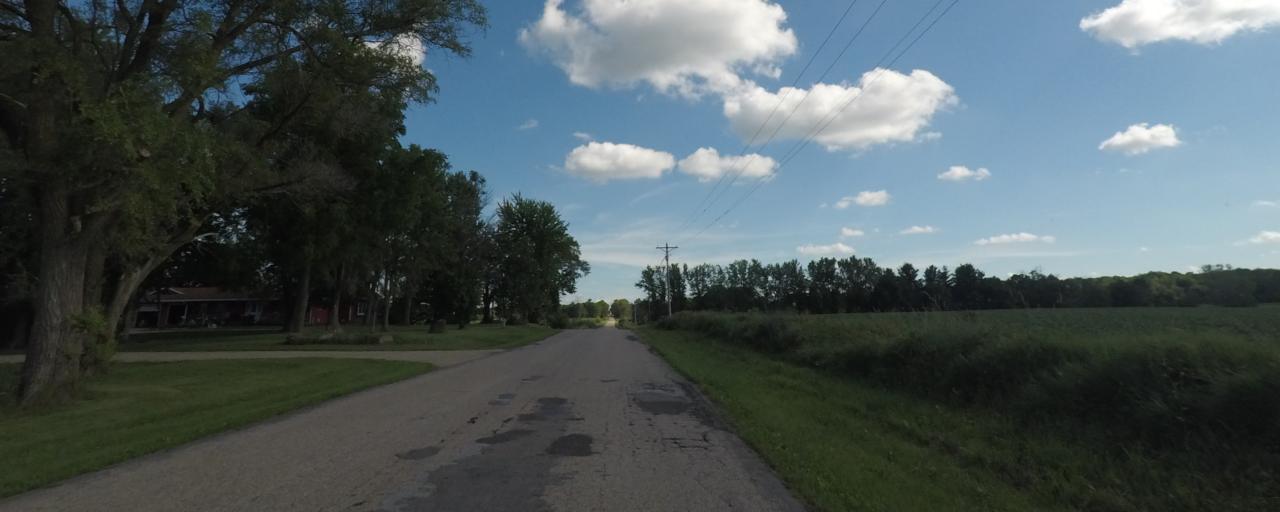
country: US
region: Wisconsin
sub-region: Rock County
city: Edgerton
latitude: 42.8381
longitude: -89.1320
